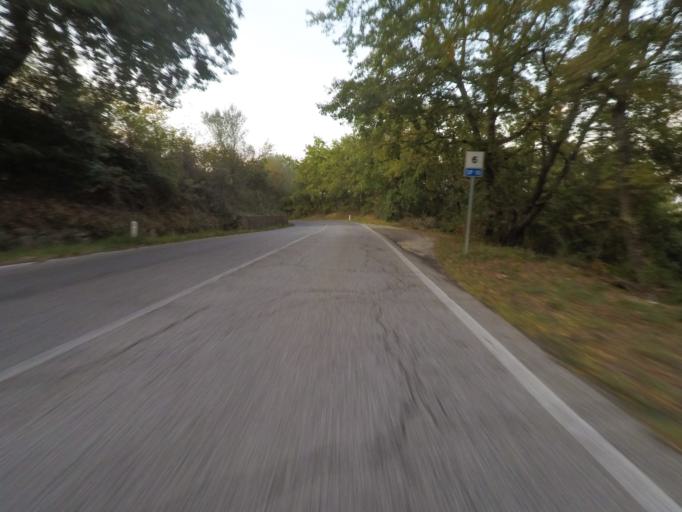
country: IT
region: Tuscany
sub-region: Provincia di Siena
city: Torrita di Siena
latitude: 43.1468
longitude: 11.7403
